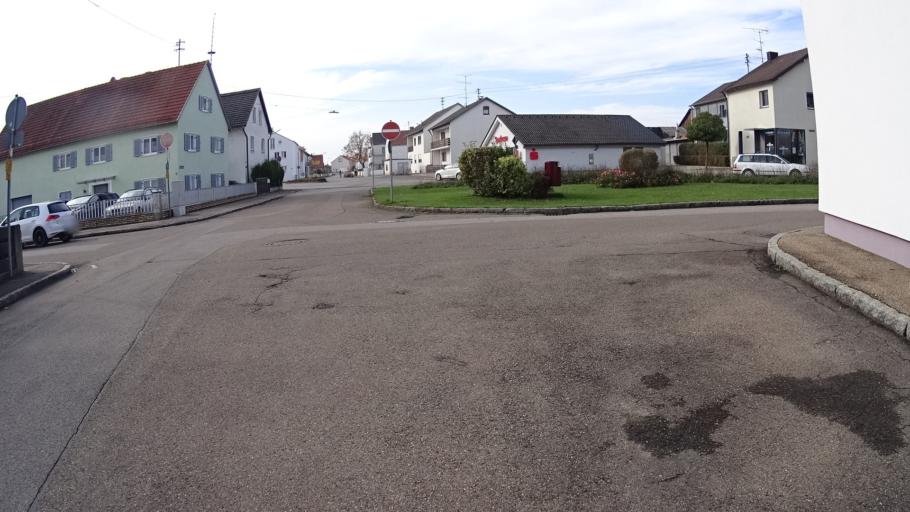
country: DE
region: Bavaria
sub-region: Upper Bavaria
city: Eitensheim
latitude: 48.8187
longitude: 11.3197
